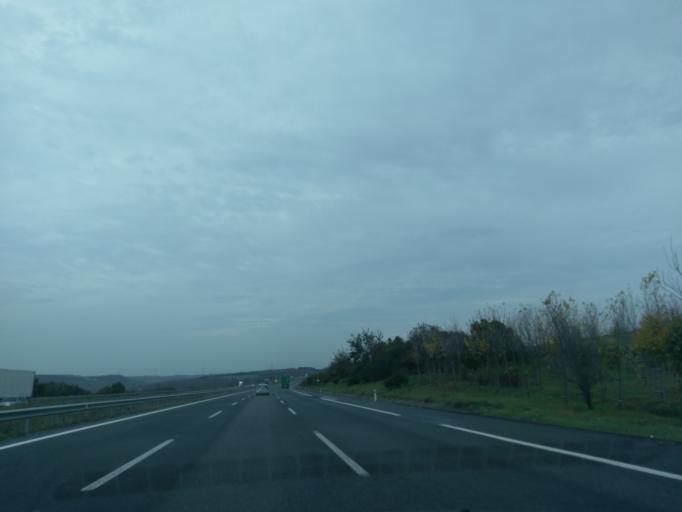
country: TR
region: Istanbul
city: Canta
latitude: 41.1706
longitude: 28.1210
